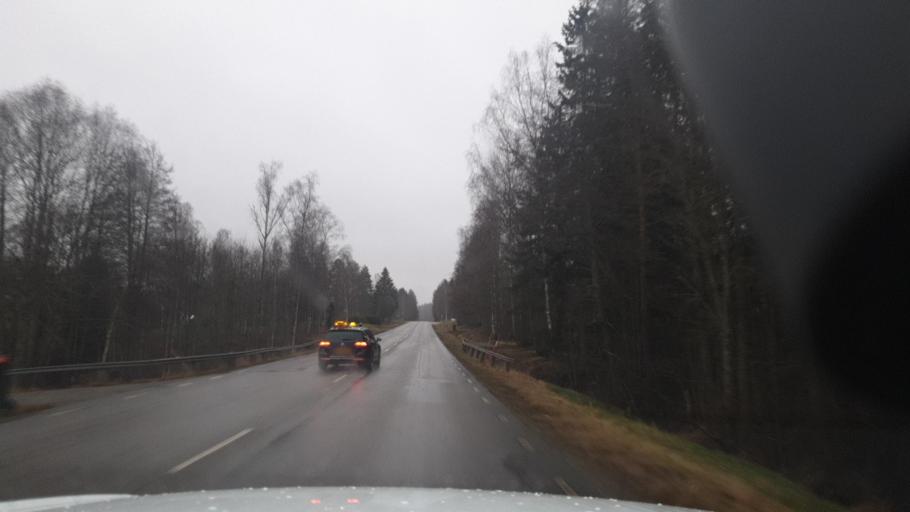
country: SE
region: Vaermland
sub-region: Arvika Kommun
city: Arvika
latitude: 59.6825
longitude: 12.6313
